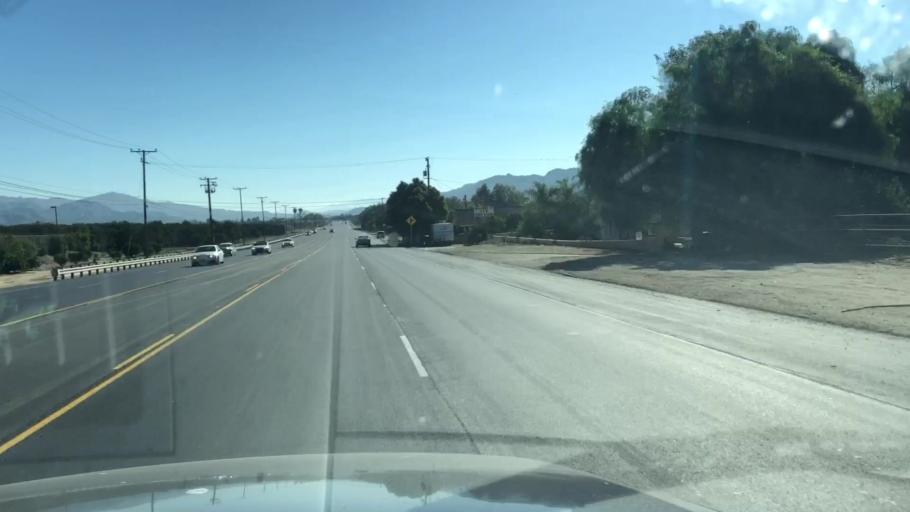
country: US
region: California
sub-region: Ventura County
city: Piru
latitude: 34.4008
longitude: -118.8262
